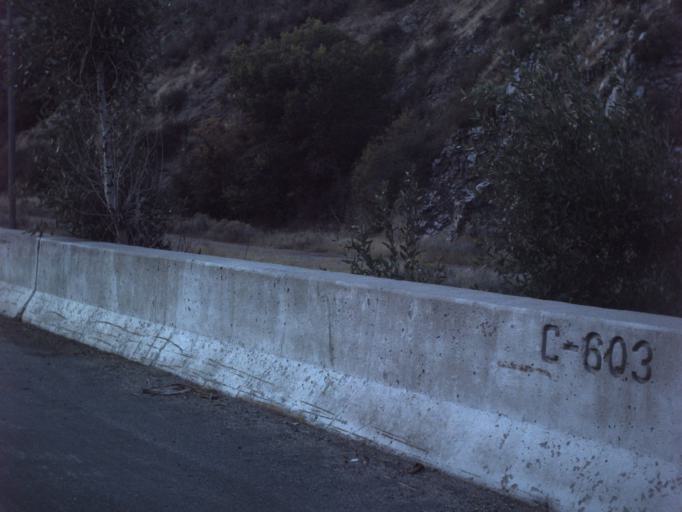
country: US
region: Utah
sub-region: Morgan County
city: Morgan
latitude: 41.0635
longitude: -111.5469
